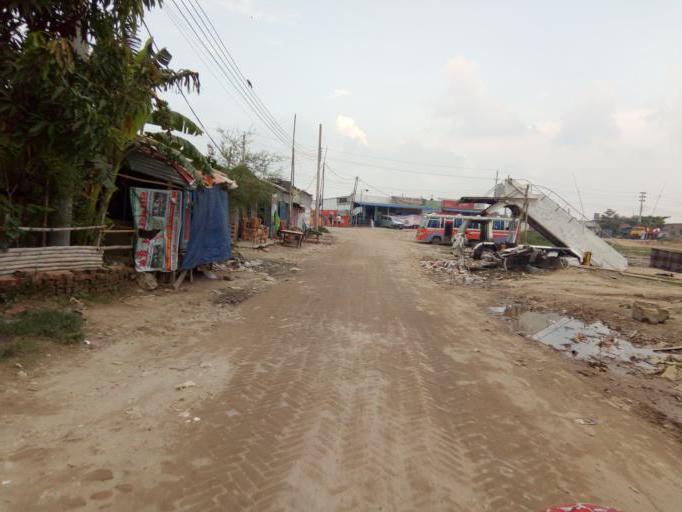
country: BD
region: Dhaka
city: Paltan
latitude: 23.7590
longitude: 90.4463
